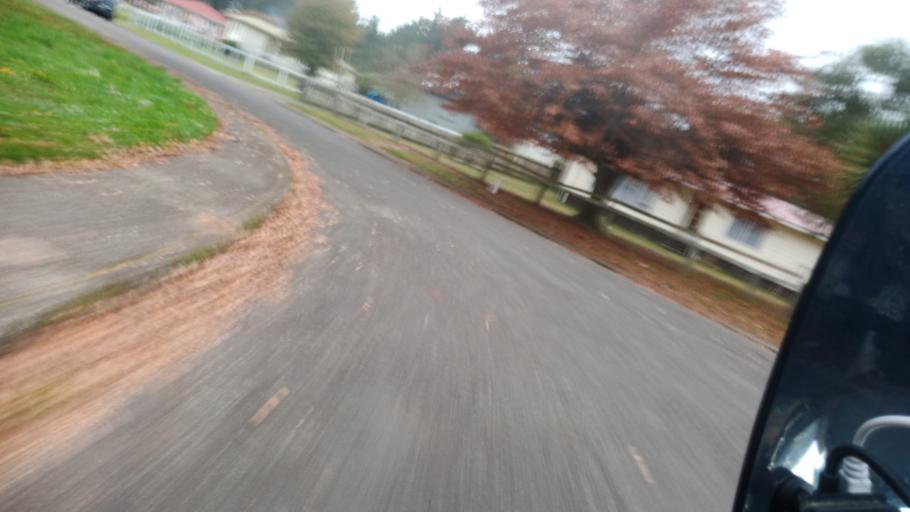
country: NZ
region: Bay of Plenty
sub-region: Whakatane District
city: Murupara
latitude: -38.6455
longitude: 176.7328
